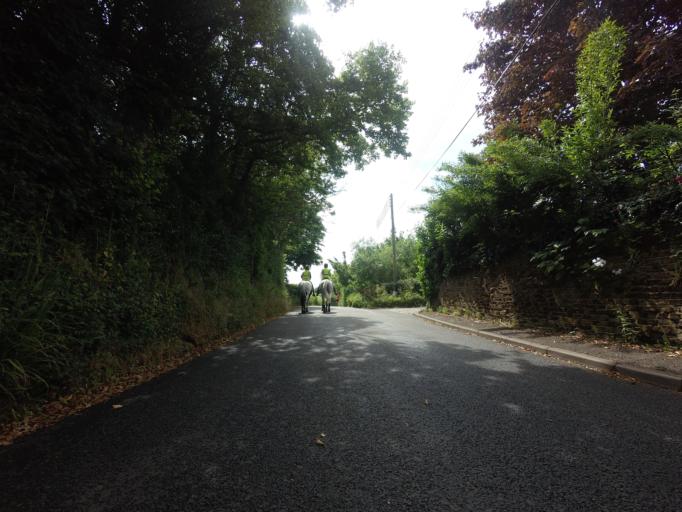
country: GB
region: England
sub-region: Kent
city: Halstead
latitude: 51.3559
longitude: 0.1338
